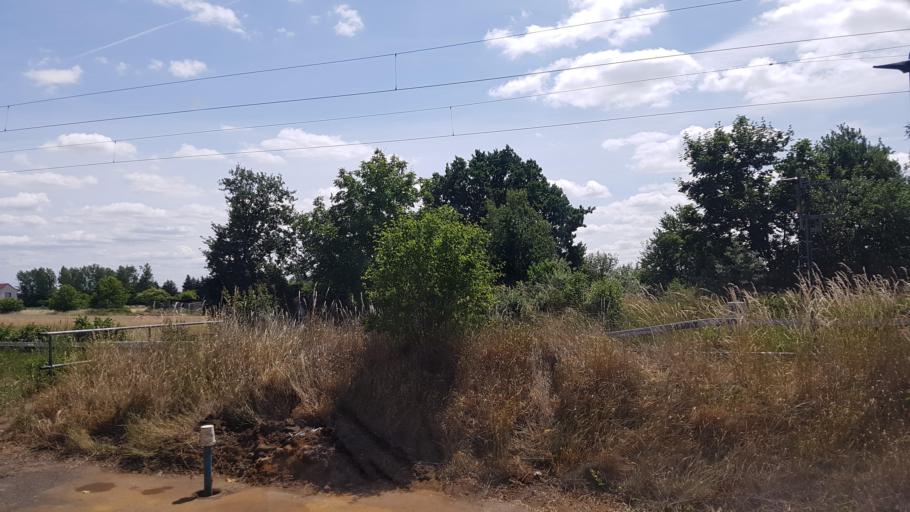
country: DE
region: Brandenburg
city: Hohenleipisch
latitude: 51.4742
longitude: 13.5636
